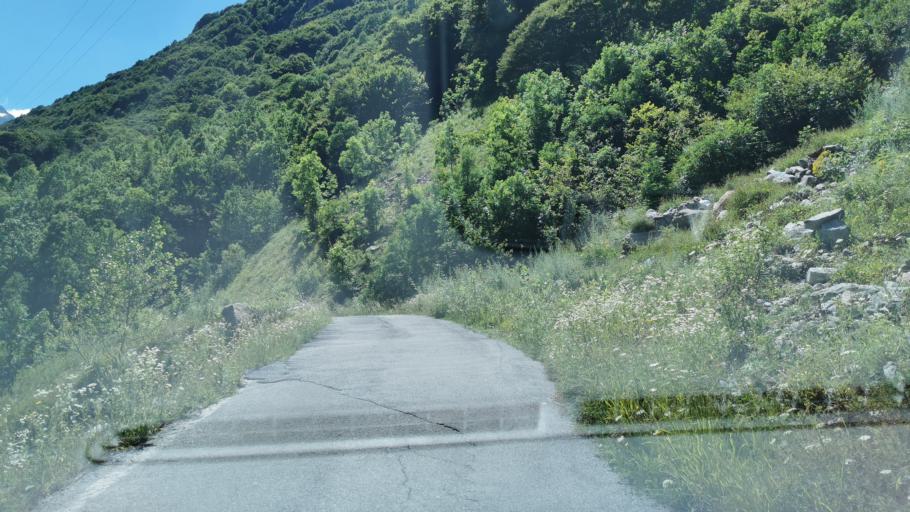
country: IT
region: Piedmont
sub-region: Provincia di Cuneo
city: Entracque
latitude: 44.1820
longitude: 7.3839
